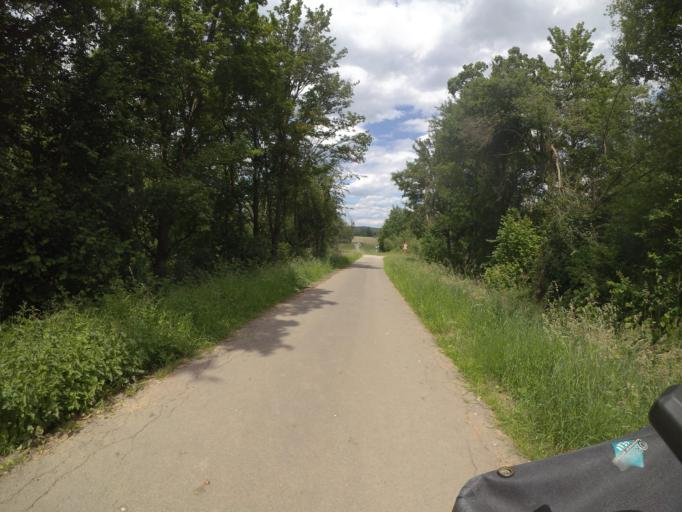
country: DE
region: Rheinland-Pfalz
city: Hauptstuhl
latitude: 49.3999
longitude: 7.4653
